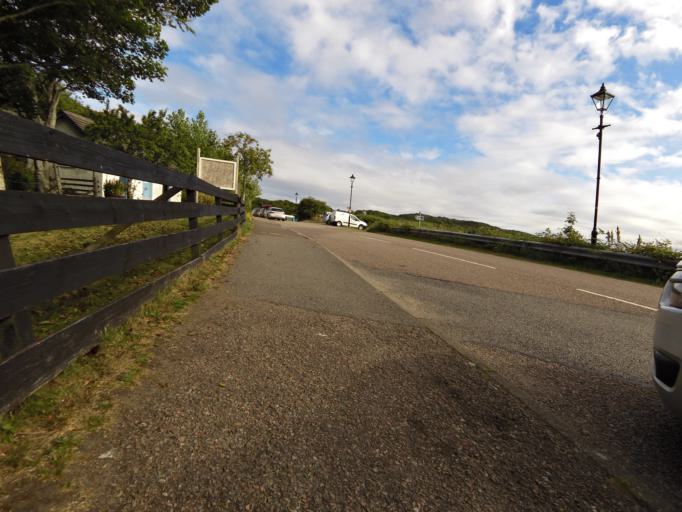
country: GB
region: Scotland
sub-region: Argyll and Bute
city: Isle Of Mull
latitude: 56.9104
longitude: -5.8479
